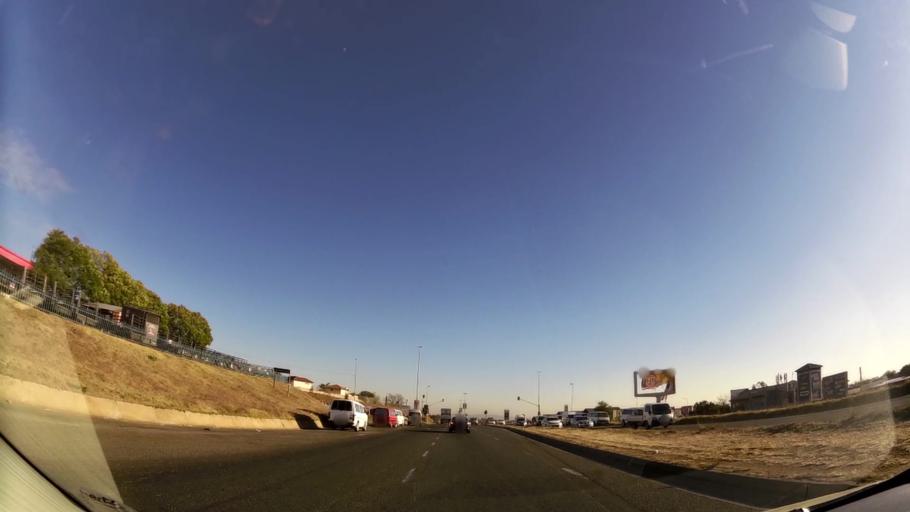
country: ZA
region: Gauteng
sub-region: West Rand District Municipality
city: Muldersdriseloop
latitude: -26.0929
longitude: 27.8706
